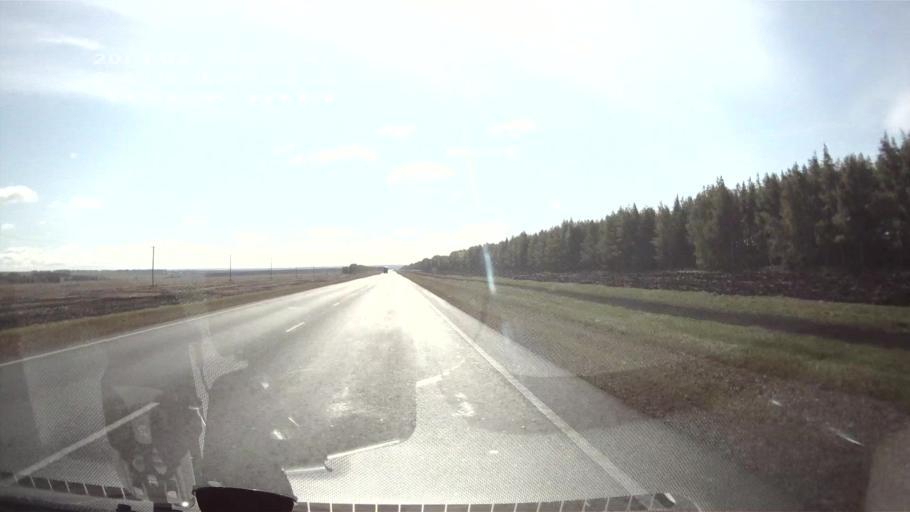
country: RU
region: Ulyanovsk
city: Tsil'na
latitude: 54.5729
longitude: 47.9042
